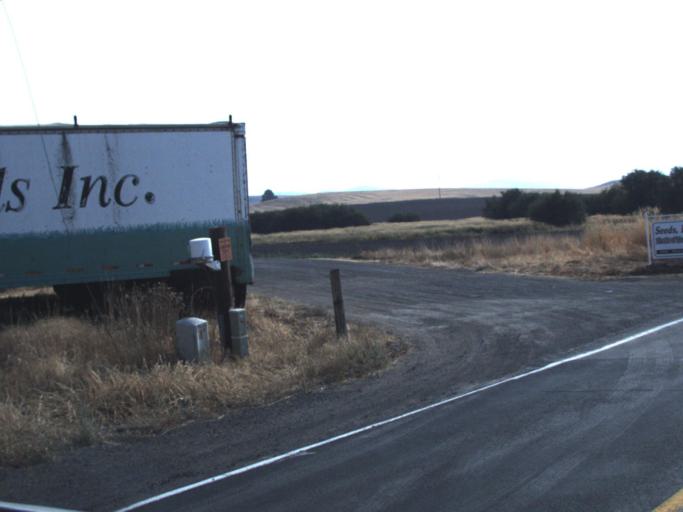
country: US
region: Idaho
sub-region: Benewah County
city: Plummer
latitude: 47.2402
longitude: -117.0400
